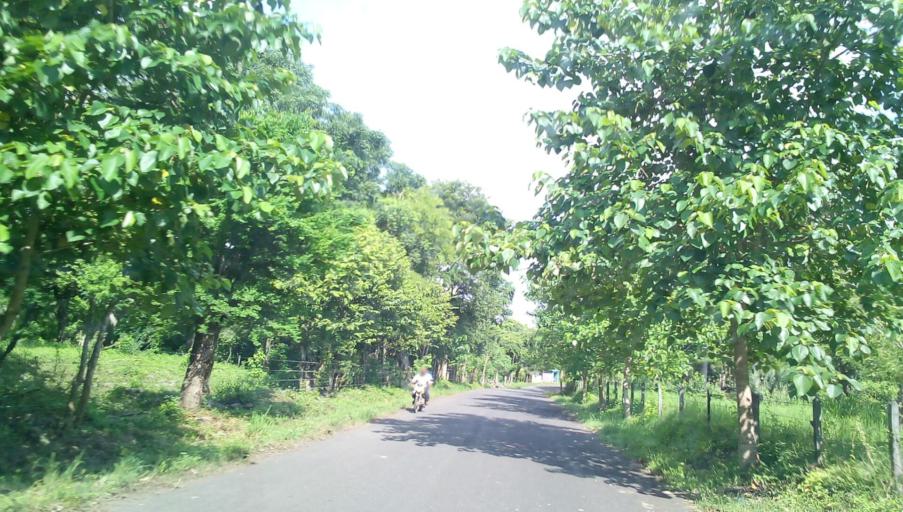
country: MX
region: Veracruz
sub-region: Citlaltepetl
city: Las Sabinas
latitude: 21.3553
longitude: -97.8987
